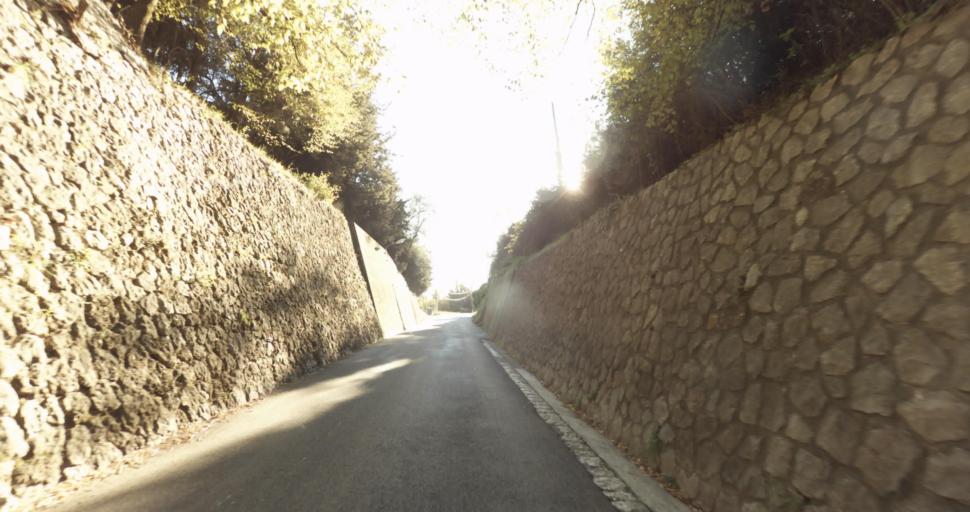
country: FR
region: Provence-Alpes-Cote d'Azur
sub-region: Departement des Alpes-Maritimes
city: Vence
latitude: 43.7345
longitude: 7.1246
